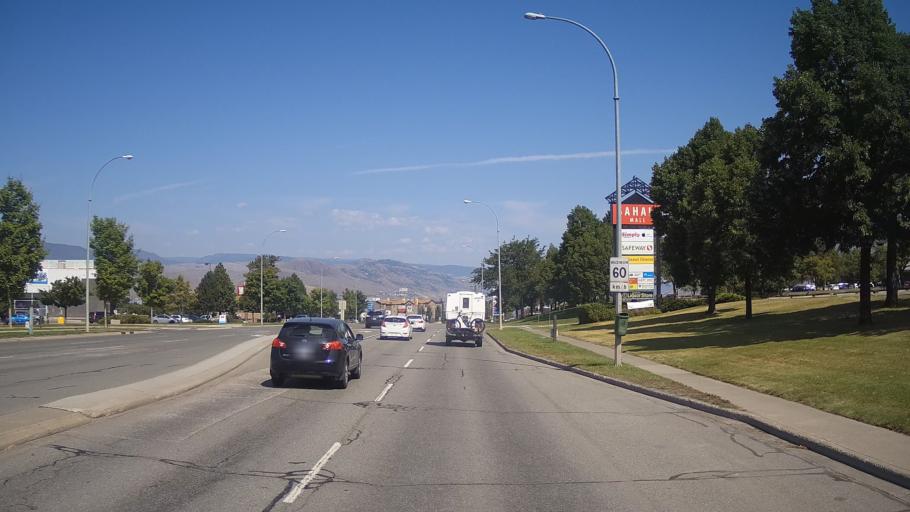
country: CA
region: British Columbia
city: Kamloops
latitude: 50.6676
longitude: -120.3542
